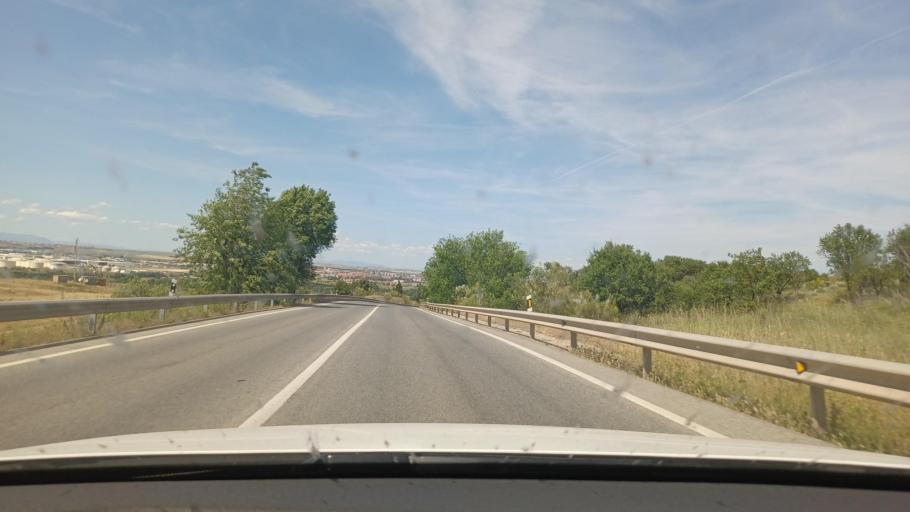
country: ES
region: Madrid
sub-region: Provincia de Madrid
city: Mejorada del Campo
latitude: 40.4129
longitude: -3.4767
